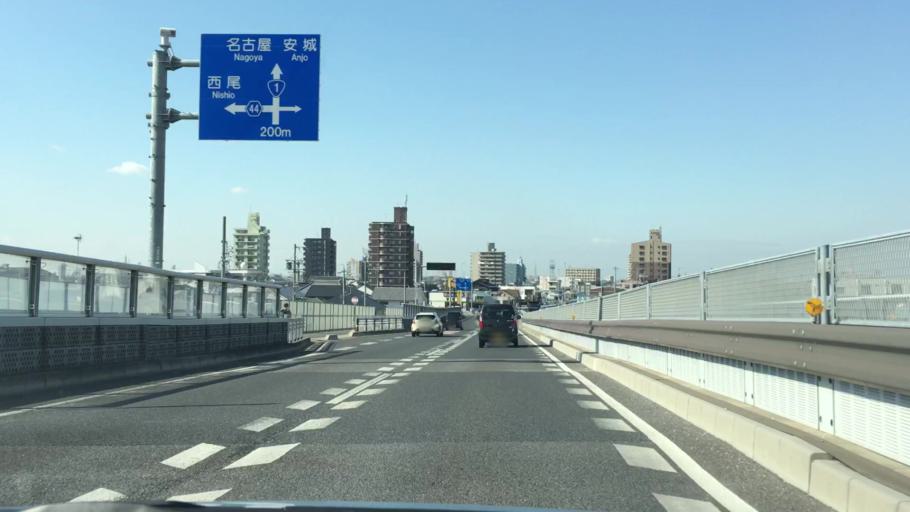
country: JP
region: Aichi
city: Okazaki
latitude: 34.9597
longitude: 137.1477
